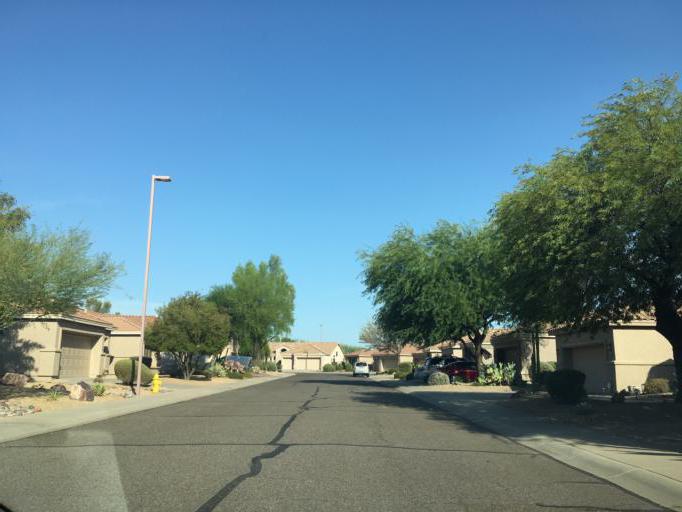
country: US
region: Arizona
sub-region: Maricopa County
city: Cave Creek
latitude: 33.6862
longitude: -111.9830
